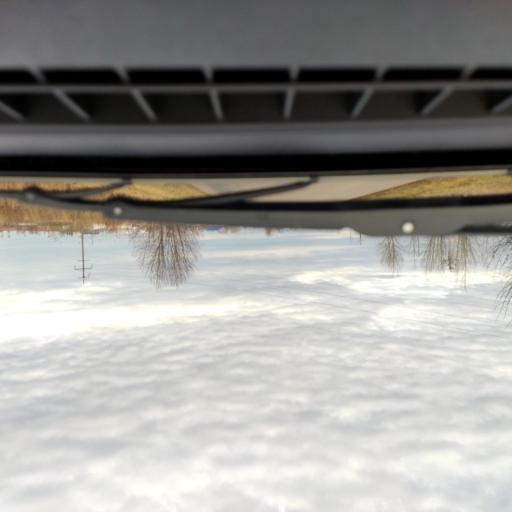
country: RU
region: Bashkortostan
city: Blagoveshchensk
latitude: 54.8937
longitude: 56.1501
